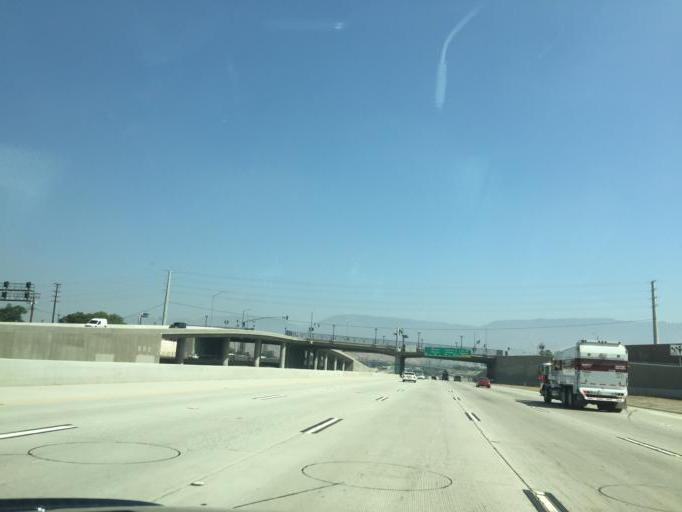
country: US
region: California
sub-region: San Bernardino County
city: San Bernardino
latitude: 34.1188
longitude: -117.3023
